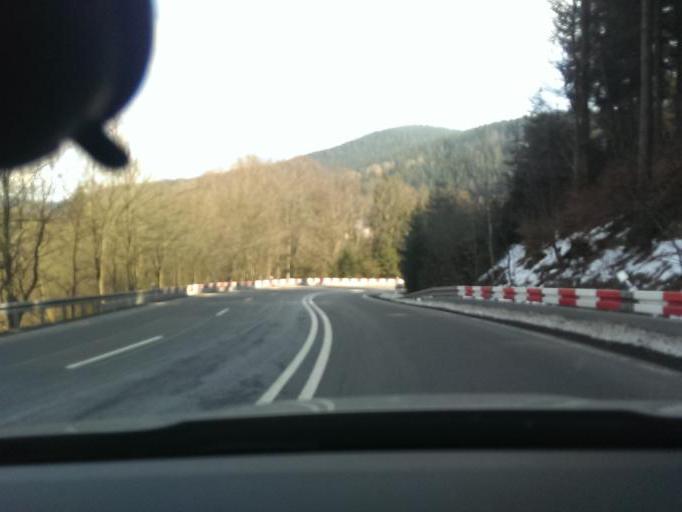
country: DE
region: Thuringia
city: Zella-Mehlis
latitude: 50.6788
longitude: 10.6851
